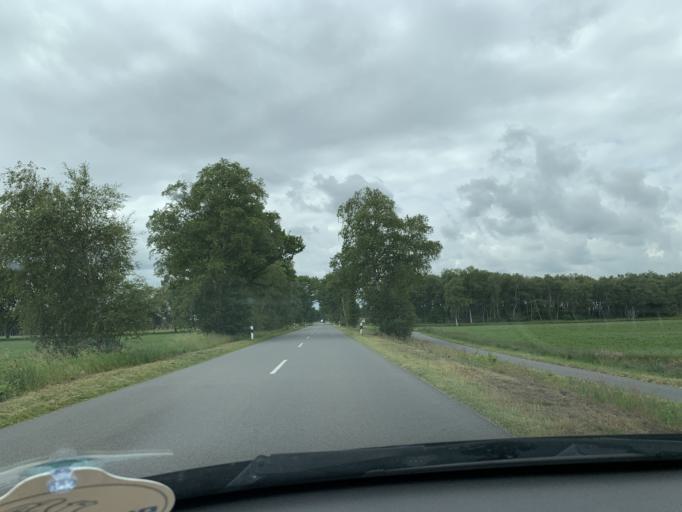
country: DE
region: Lower Saxony
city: Bockhorn
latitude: 53.3235
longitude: 8.0206
